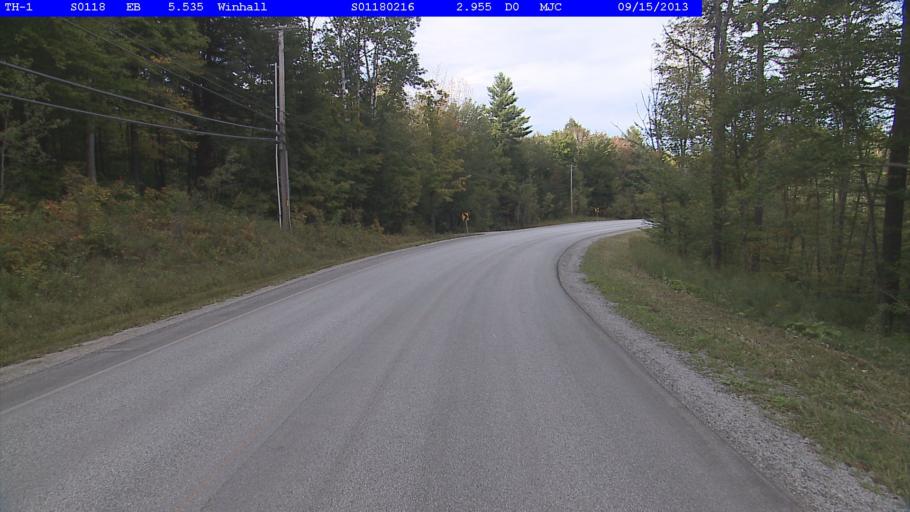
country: US
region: Vermont
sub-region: Bennington County
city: Manchester Center
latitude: 43.1401
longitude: -72.8832
